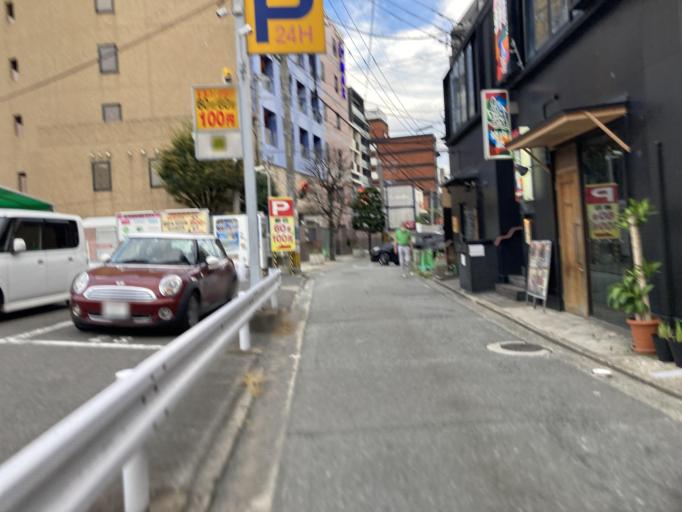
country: JP
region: Fukuoka
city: Fukuoka-shi
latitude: 33.5888
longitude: 130.4082
